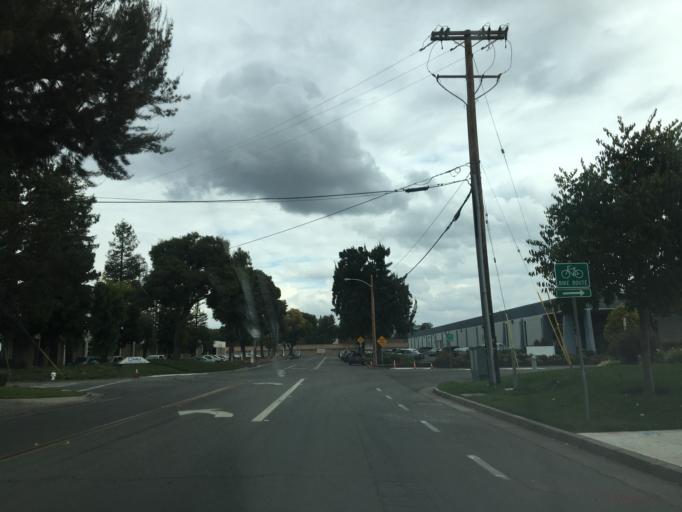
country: US
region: California
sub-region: Santa Clara County
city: Sunnyvale
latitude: 37.4064
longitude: -121.9891
